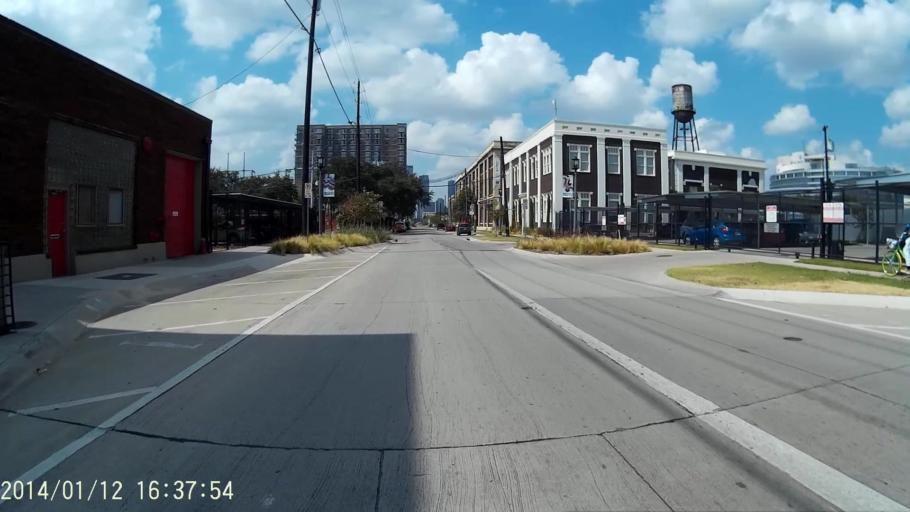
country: US
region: Texas
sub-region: Dallas County
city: Dallas
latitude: 32.7862
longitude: -96.7757
